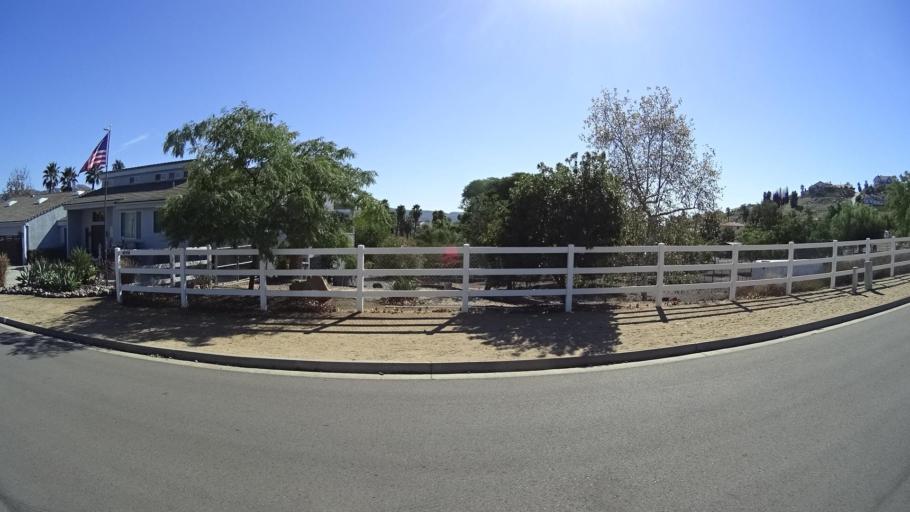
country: US
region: California
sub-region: San Diego County
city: Lakeside
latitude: 32.8705
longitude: -116.8650
